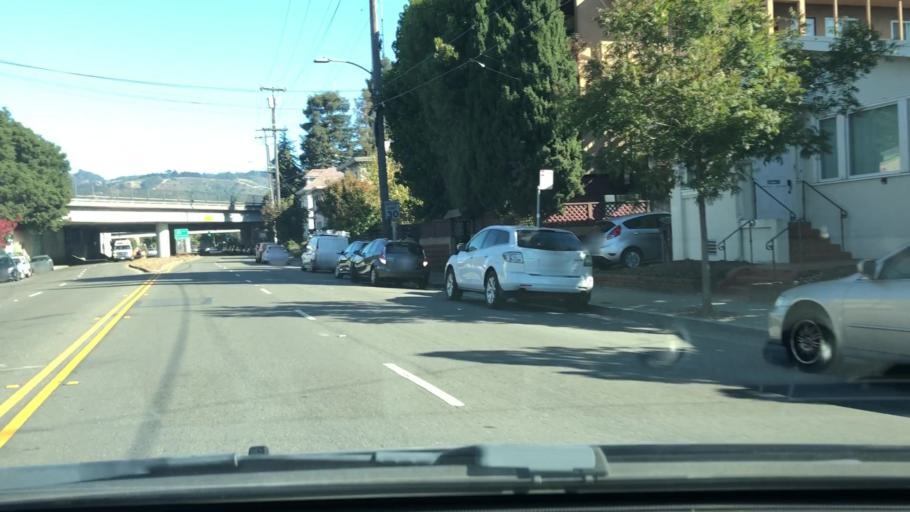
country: US
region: California
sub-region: Alameda County
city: Emeryville
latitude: 37.8412
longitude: -122.2589
